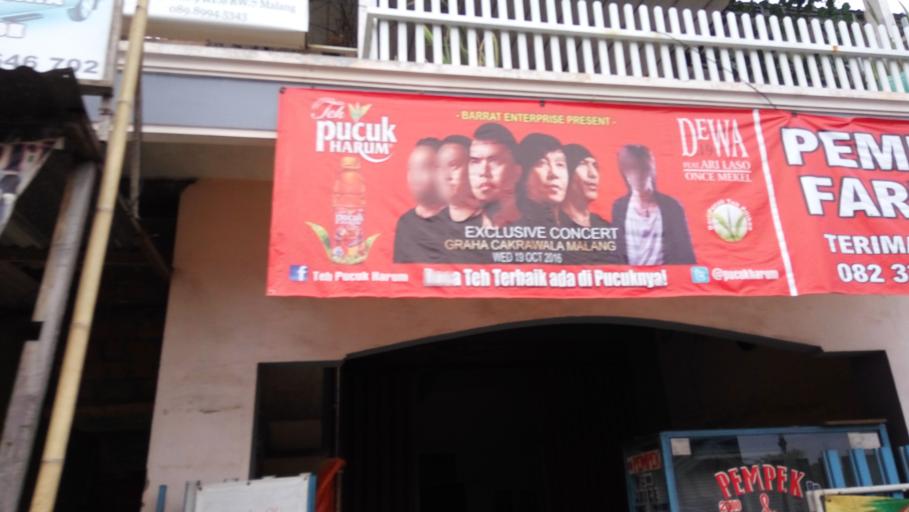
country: ID
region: East Java
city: Malang
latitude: -7.9238
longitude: 112.5983
